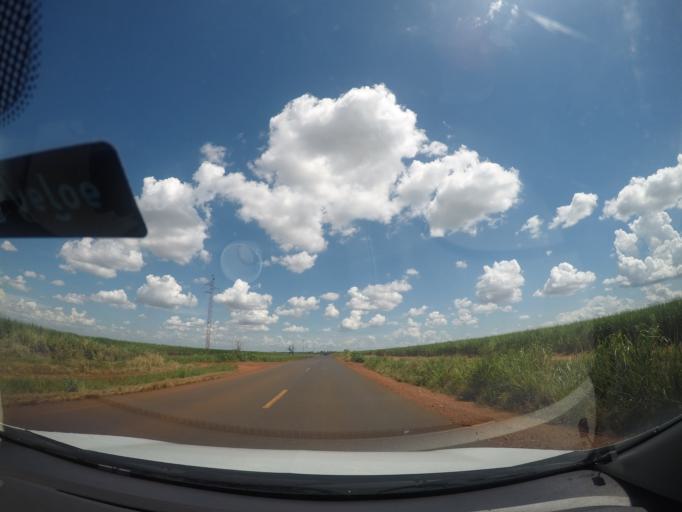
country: BR
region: Minas Gerais
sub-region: Frutal
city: Frutal
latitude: -19.8245
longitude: -48.7328
